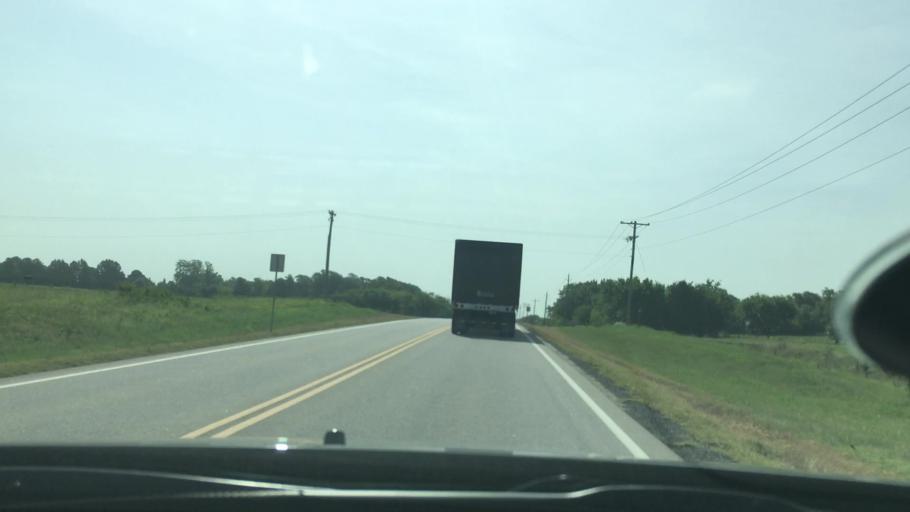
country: US
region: Oklahoma
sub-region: Atoka County
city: Atoka
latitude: 34.3976
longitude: -96.1665
